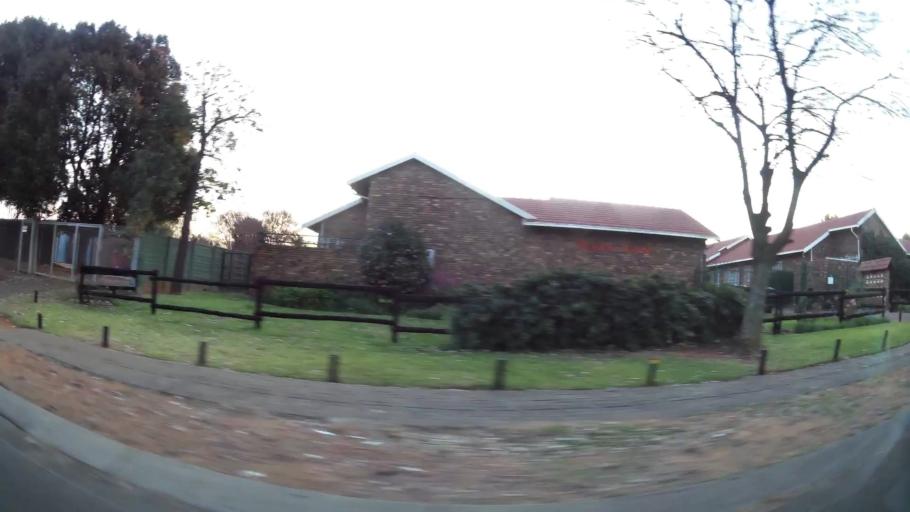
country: ZA
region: Gauteng
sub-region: City of Johannesburg Metropolitan Municipality
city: Modderfontein
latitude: -26.0666
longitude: 28.2293
